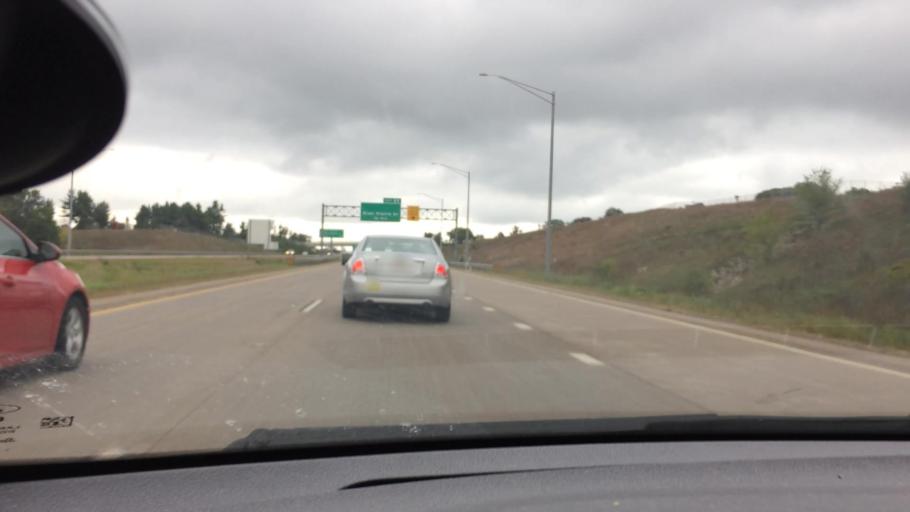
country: US
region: Wisconsin
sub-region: Eau Claire County
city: Altoona
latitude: 44.8022
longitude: -91.4553
